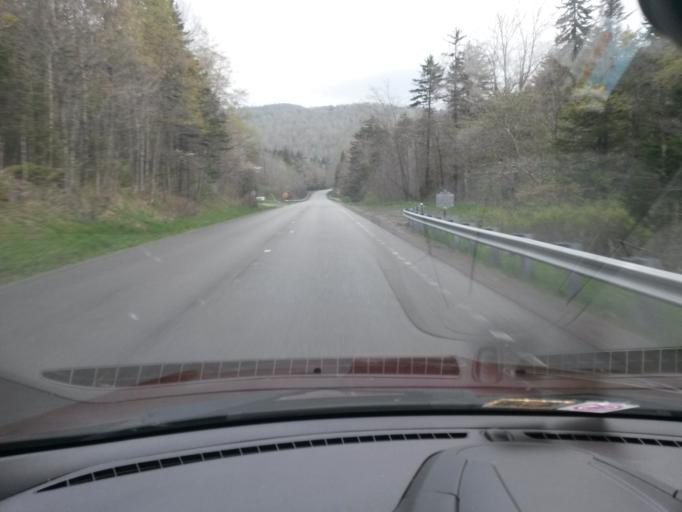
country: US
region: West Virginia
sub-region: Randolph County
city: Elkins
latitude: 38.6121
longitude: -79.8672
